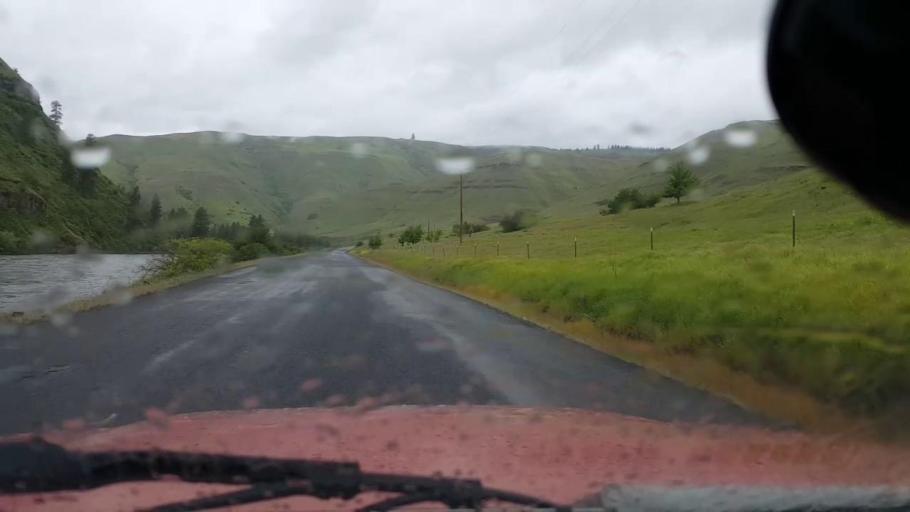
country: US
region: Washington
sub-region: Asotin County
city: Asotin
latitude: 46.0370
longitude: -117.2807
